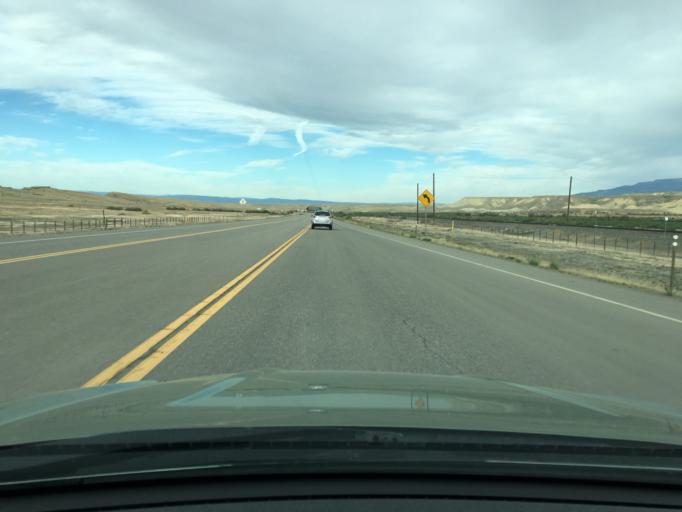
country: US
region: Colorado
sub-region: Delta County
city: Orchard City
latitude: 38.8013
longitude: -107.9032
